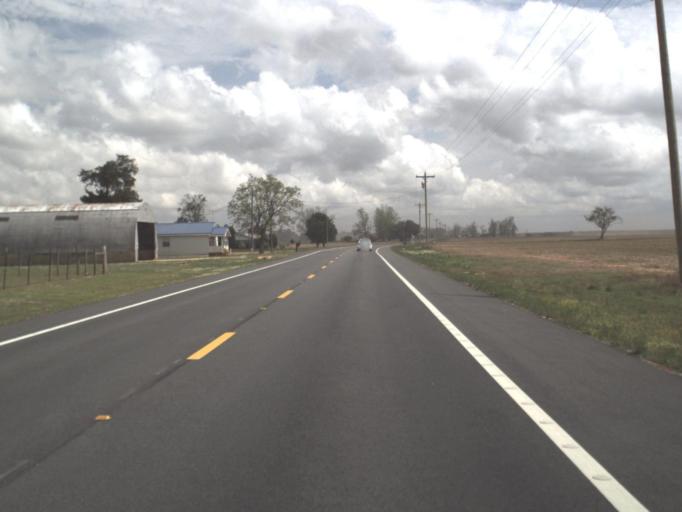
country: US
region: Florida
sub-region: Escambia County
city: Century
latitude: 30.8908
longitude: -87.1649
